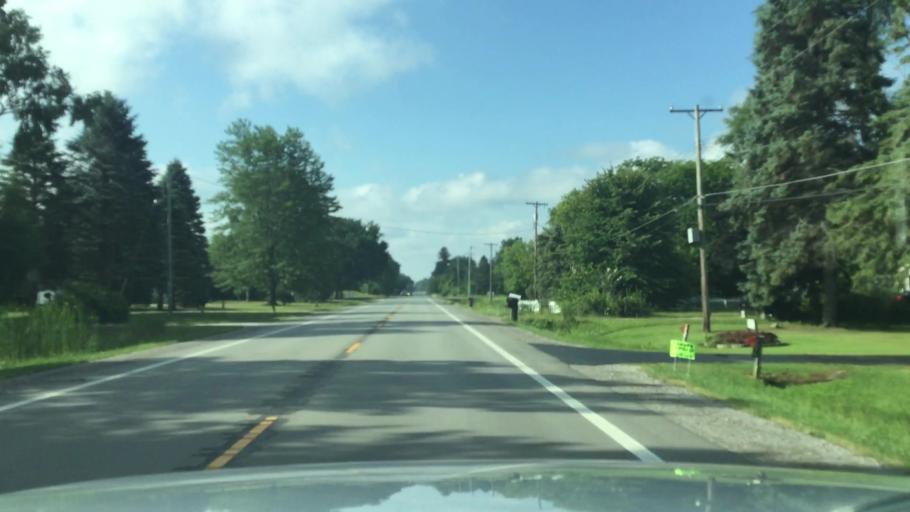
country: US
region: Michigan
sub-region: Genesee County
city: Clio
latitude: 43.2378
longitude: -83.7353
